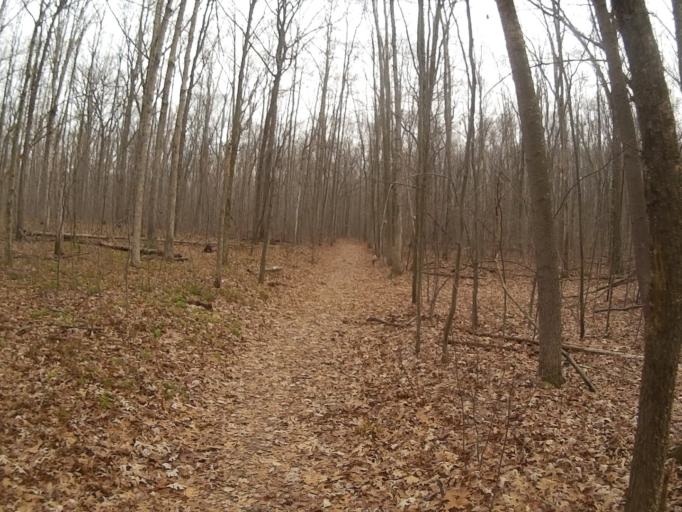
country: US
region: Pennsylvania
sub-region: Centre County
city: Park Forest Village
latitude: 40.7880
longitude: -77.9244
